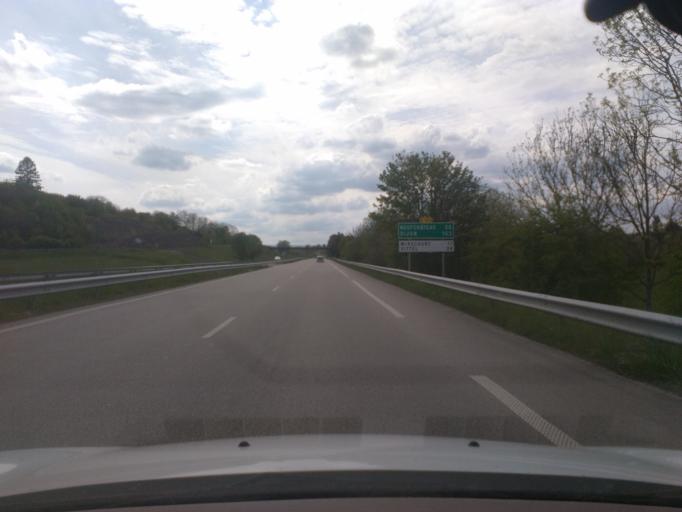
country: FR
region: Lorraine
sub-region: Departement des Vosges
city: Darnieulles
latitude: 48.2191
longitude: 6.2377
